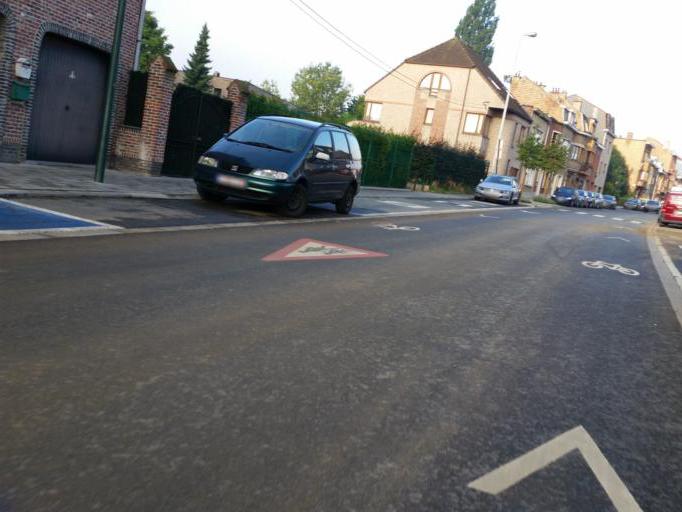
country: BE
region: Flanders
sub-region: Provincie Vlaams-Brabant
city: Grimbergen
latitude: 50.8937
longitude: 4.3765
